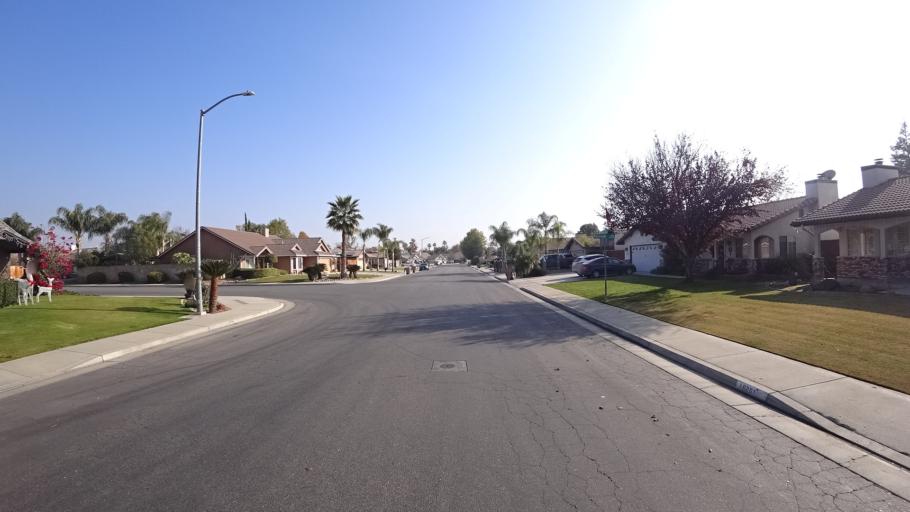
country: US
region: California
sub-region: Kern County
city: Greenacres
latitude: 35.4085
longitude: -119.1158
